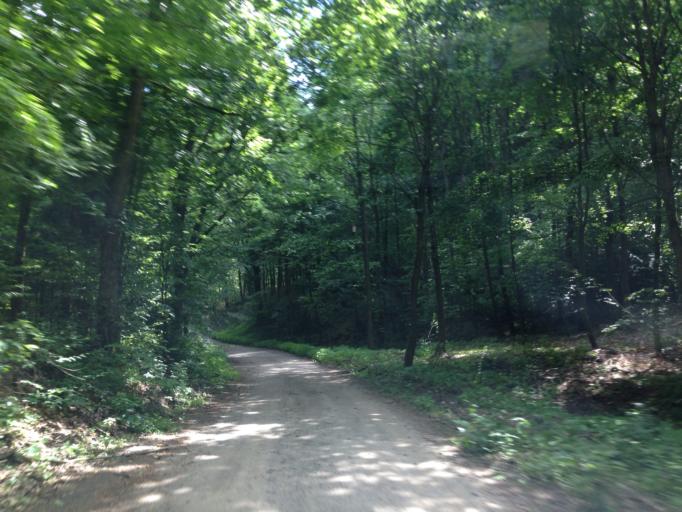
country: PL
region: Kujawsko-Pomorskie
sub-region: Powiat brodnicki
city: Gorzno
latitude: 53.2193
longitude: 19.6516
